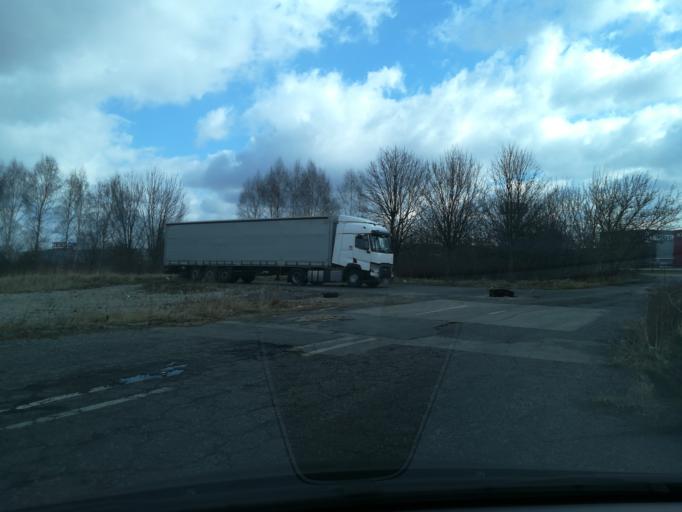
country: PL
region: Silesian Voivodeship
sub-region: Czestochowa
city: Czestochowa
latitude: 50.8220
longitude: 19.1388
